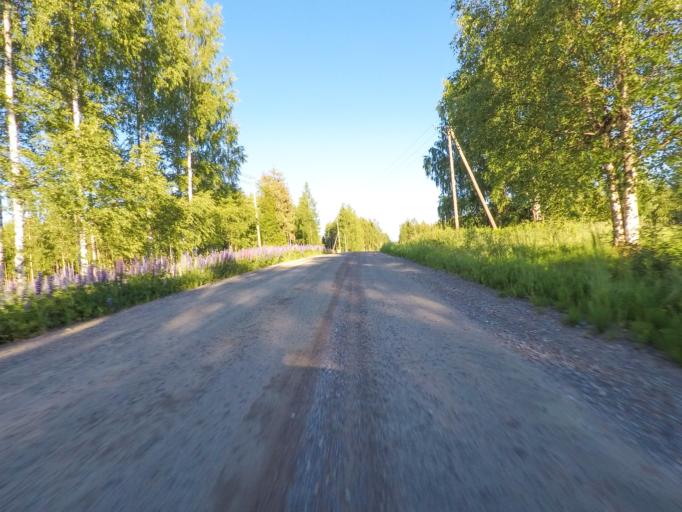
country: FI
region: Northern Savo
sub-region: Kuopio
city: Maaninka
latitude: 62.8772
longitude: 27.3007
